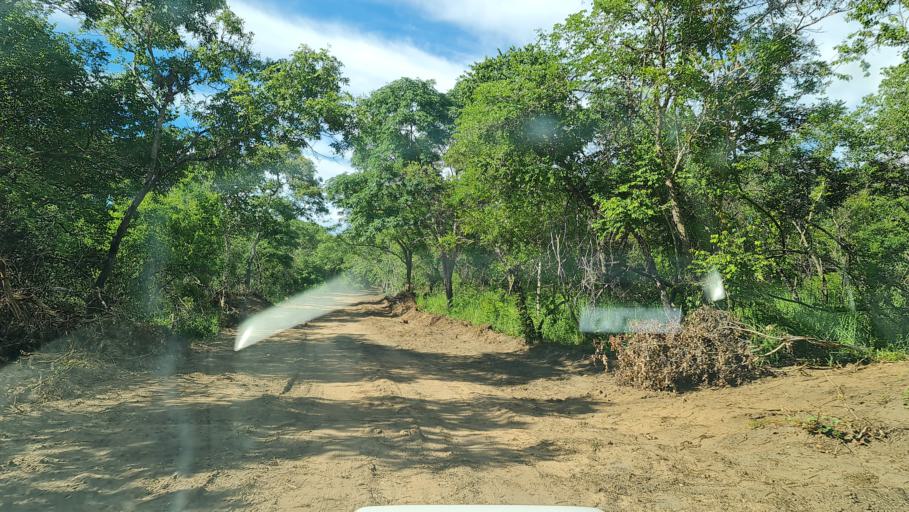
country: MZ
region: Nampula
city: Antonio Enes
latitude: -15.5307
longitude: 40.1263
